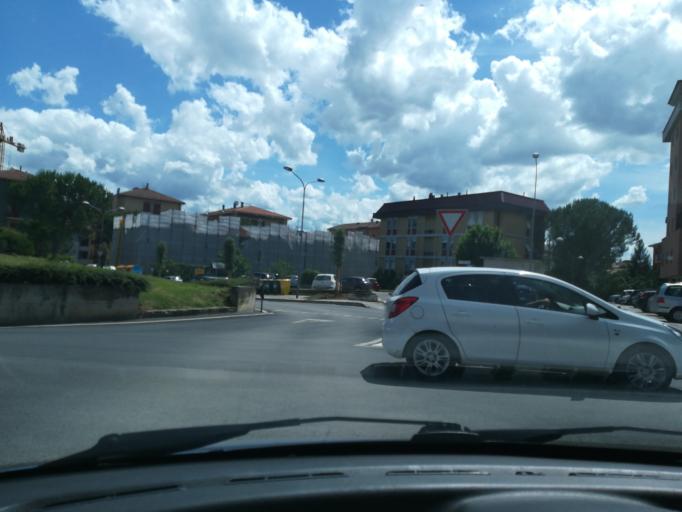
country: IT
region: The Marches
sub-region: Provincia di Macerata
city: Tolentino
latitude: 43.2132
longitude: 13.2908
